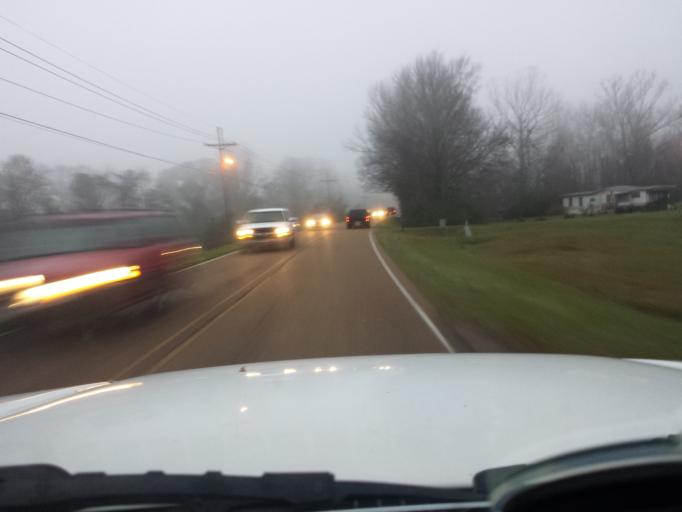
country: US
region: Mississippi
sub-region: Rankin County
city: Flowood
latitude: 32.3346
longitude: -90.0831
